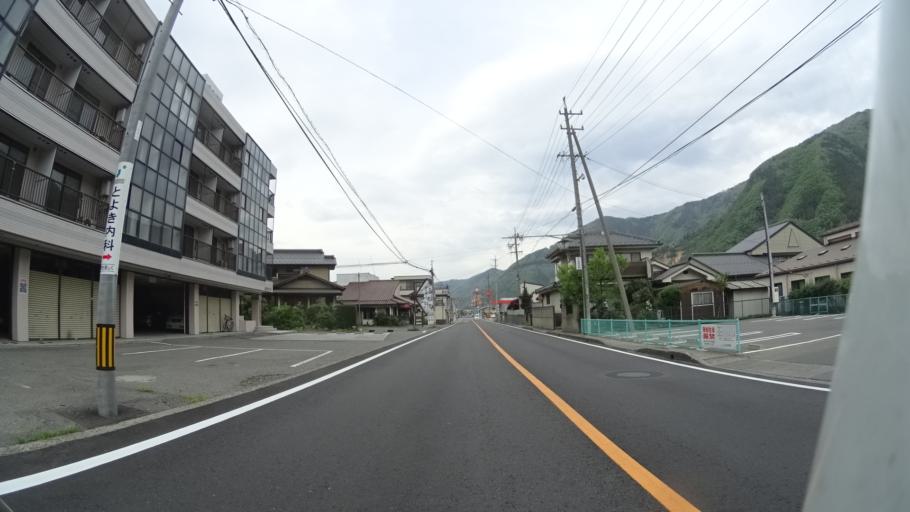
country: JP
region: Nagano
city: Ueda
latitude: 36.4837
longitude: 138.1543
